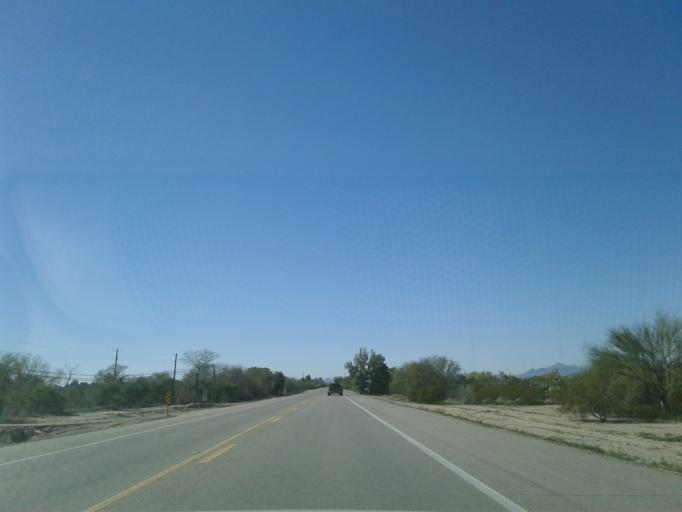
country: US
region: Arizona
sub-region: Pima County
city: Avra Valley
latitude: 32.4580
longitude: -111.2760
